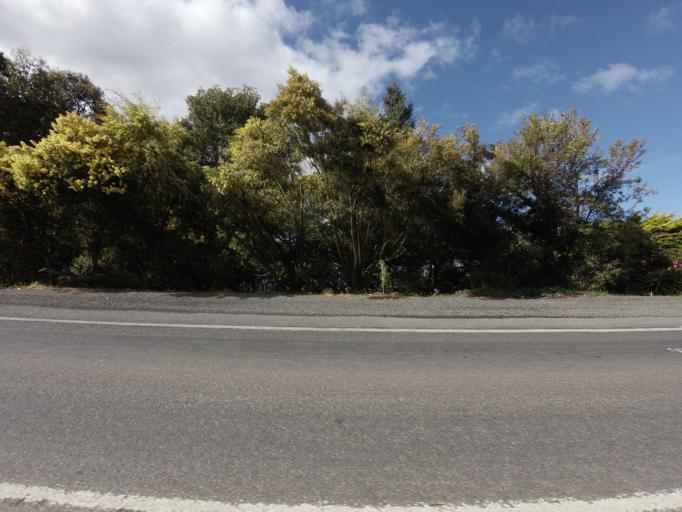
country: AU
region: Tasmania
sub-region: Huon Valley
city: Geeveston
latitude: -43.1447
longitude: 146.9774
